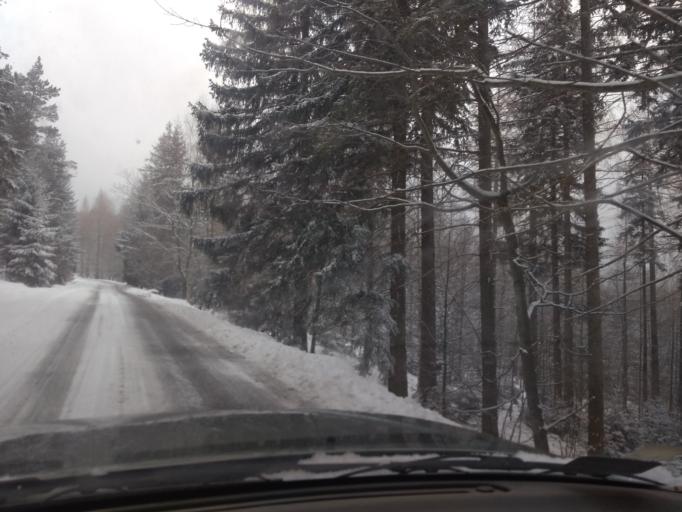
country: PL
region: Lower Silesian Voivodeship
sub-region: Powiat jeleniogorski
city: Sosnowka
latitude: 50.7892
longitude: 15.7162
